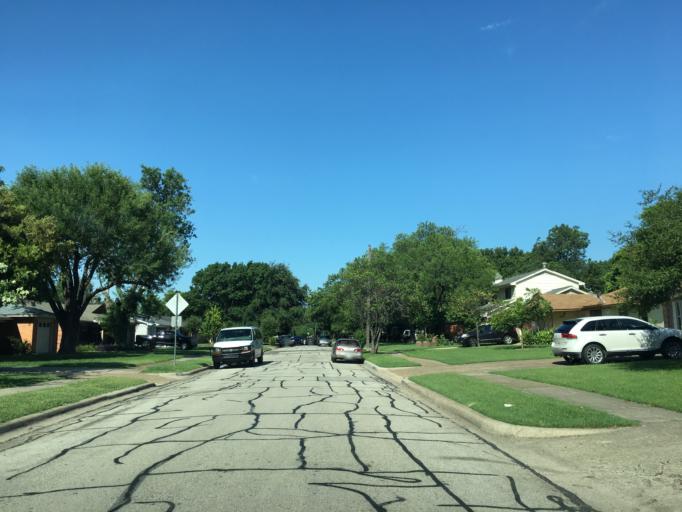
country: US
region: Texas
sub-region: Dallas County
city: Farmers Branch
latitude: 32.9166
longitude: -96.8705
